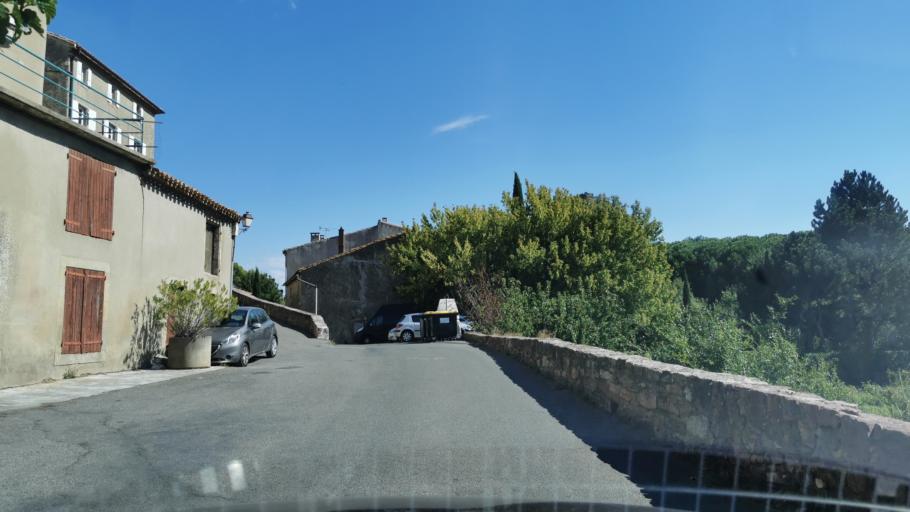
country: FR
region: Languedoc-Roussillon
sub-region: Departement de l'Aude
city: Caunes-Minervois
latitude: 43.3256
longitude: 2.5293
